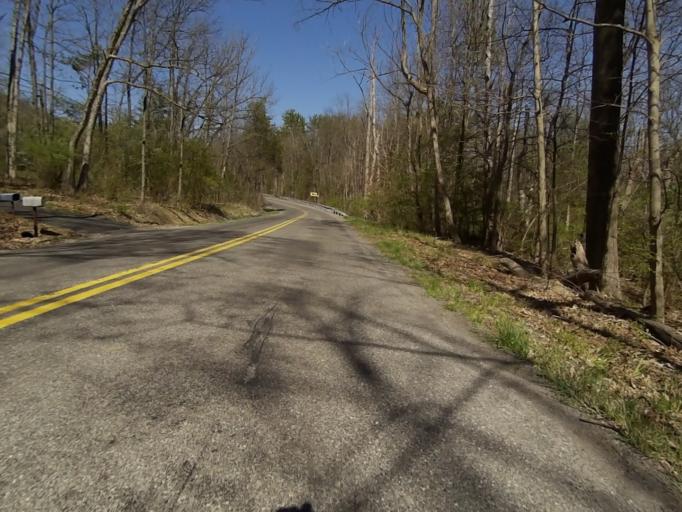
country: US
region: Pennsylvania
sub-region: Centre County
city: Houserville
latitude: 40.8816
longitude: -77.8652
